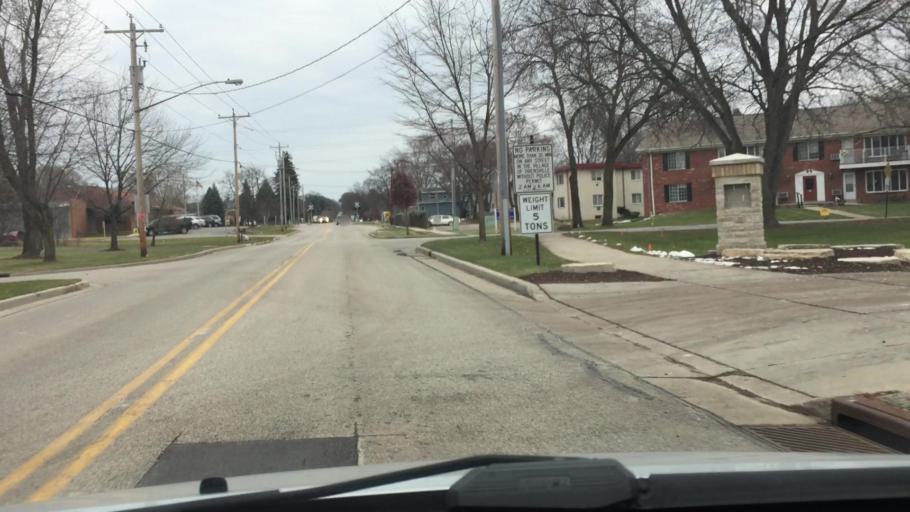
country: US
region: Wisconsin
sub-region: Ozaukee County
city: Mequon
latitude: 43.2362
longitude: -87.9887
